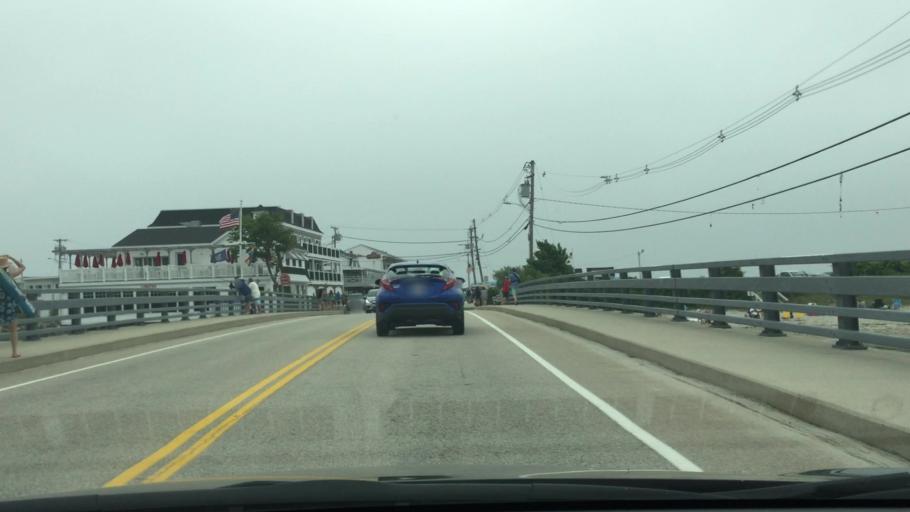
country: US
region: Maine
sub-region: York County
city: Ogunquit
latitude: 43.2502
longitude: -70.5959
